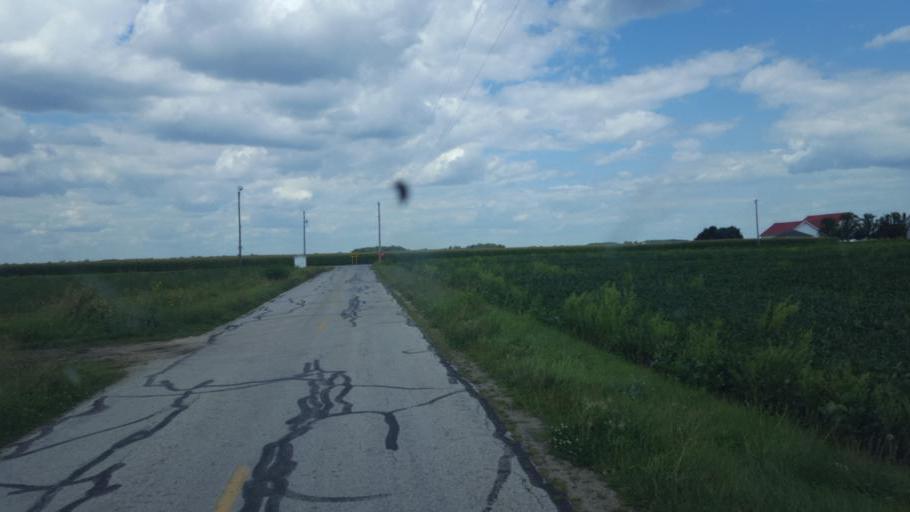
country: US
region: Ohio
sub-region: Ottawa County
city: Elmore
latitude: 41.5005
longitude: -83.2894
